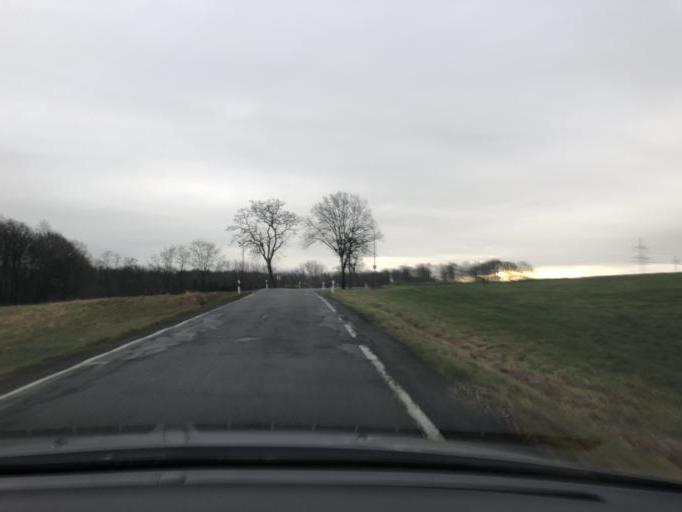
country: DE
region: Saxony
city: Niederfrohna
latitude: 50.8822
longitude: 12.7149
